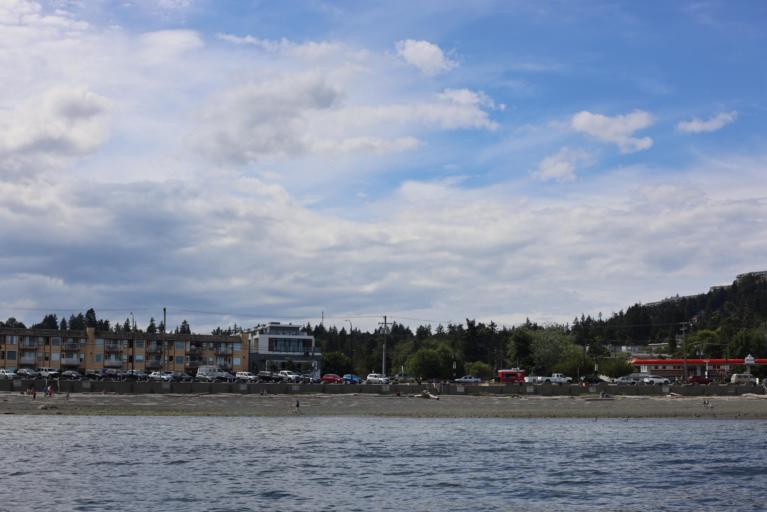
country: CA
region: British Columbia
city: Nanaimo
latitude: 49.2051
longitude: -123.9673
